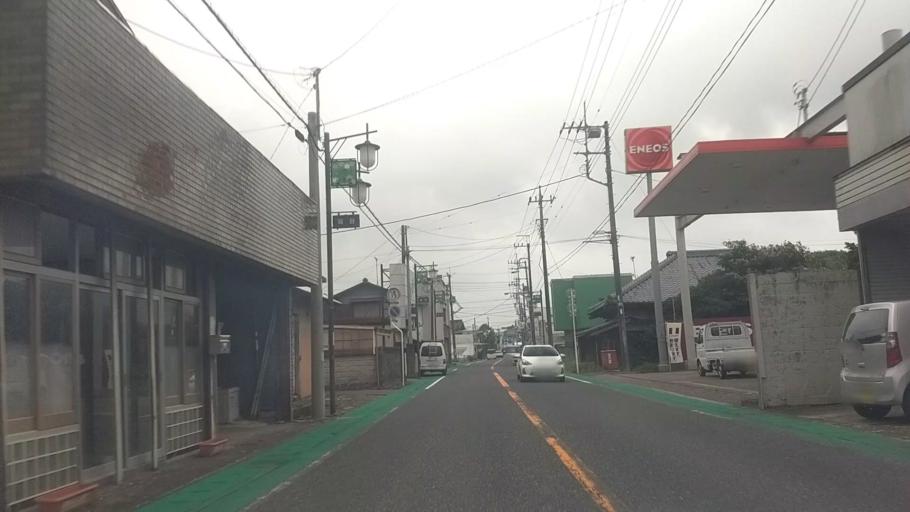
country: JP
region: Chiba
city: Ohara
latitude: 35.2811
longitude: 140.3091
